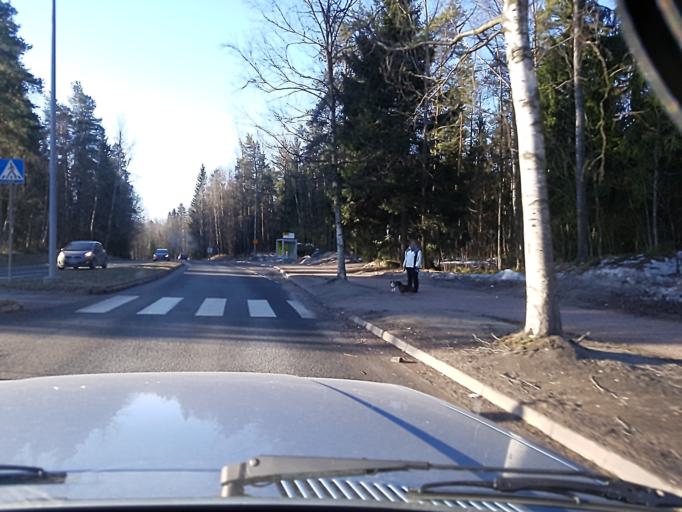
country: FI
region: Uusimaa
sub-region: Helsinki
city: Kilo
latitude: 60.2767
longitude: 24.8357
